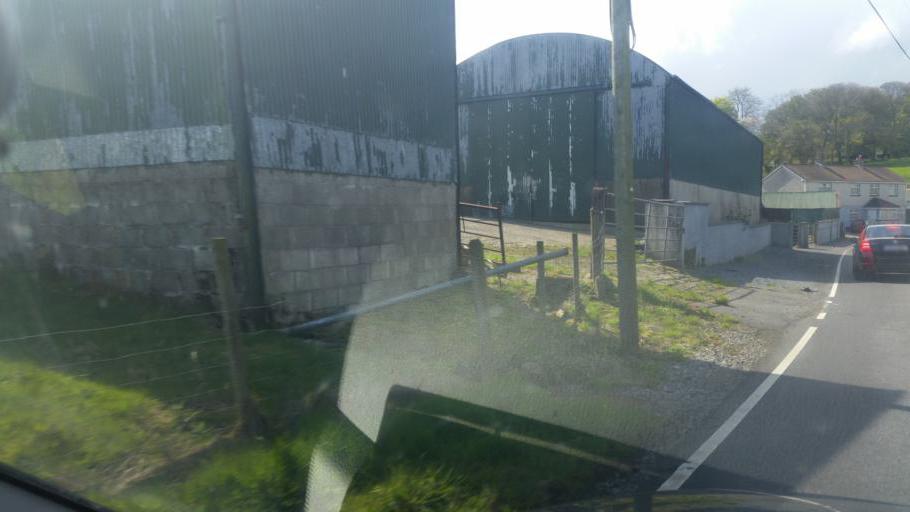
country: GB
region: Northern Ireland
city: Irvinestown
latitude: 54.4481
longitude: -7.7965
